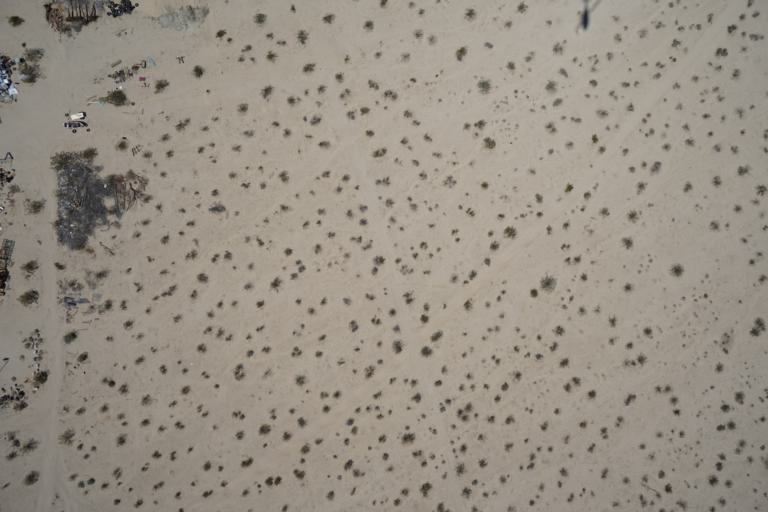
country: US
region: California
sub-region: San Bernardino County
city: Twentynine Palms
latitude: 34.1301
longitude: -116.0333
